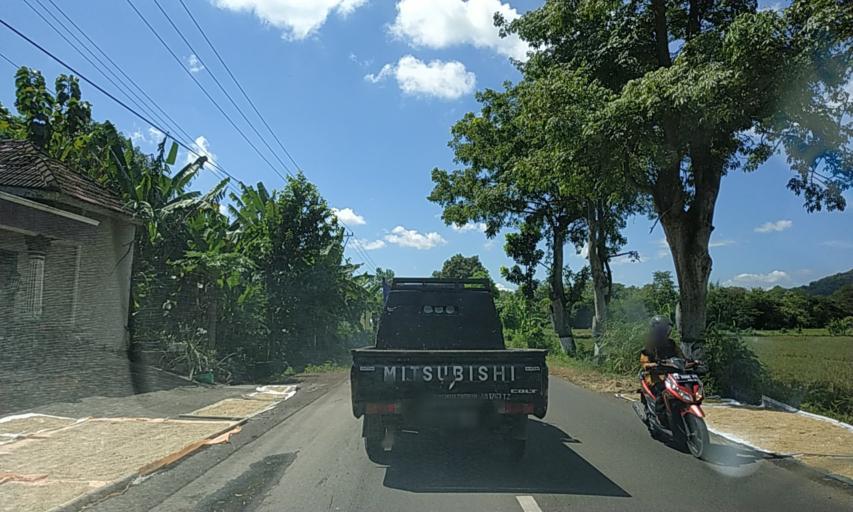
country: ID
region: Central Java
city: Trucuk
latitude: -7.7438
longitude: 110.7556
